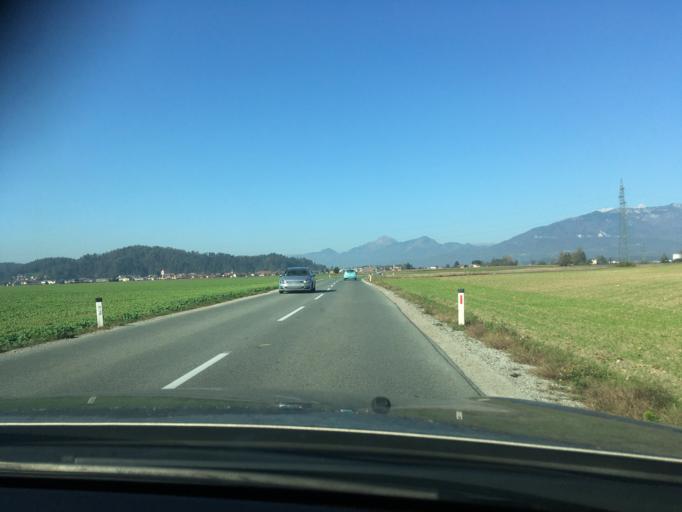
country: SI
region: Domzale
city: Domzale
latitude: 46.1537
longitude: 14.5879
